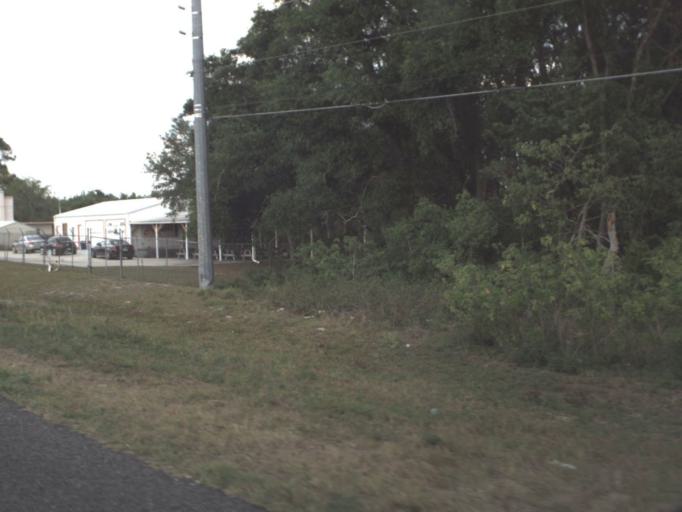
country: US
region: Florida
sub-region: Lake County
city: Eustis
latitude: 28.8851
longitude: -81.6870
